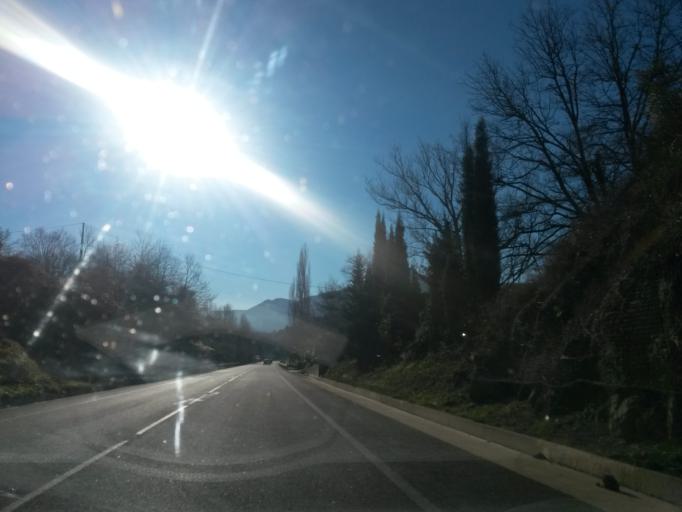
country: ES
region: Catalonia
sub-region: Provincia de Girona
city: Bas
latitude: 42.1093
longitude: 2.4906
